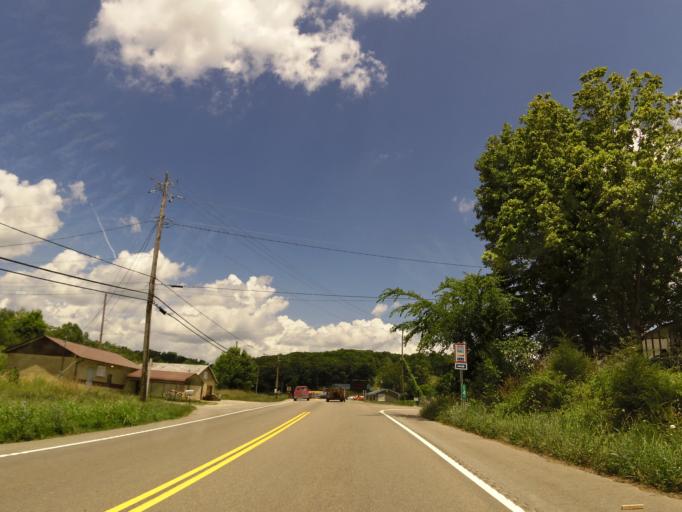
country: US
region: Tennessee
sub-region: Union County
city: Maynardville
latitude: 36.3108
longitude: -83.7530
